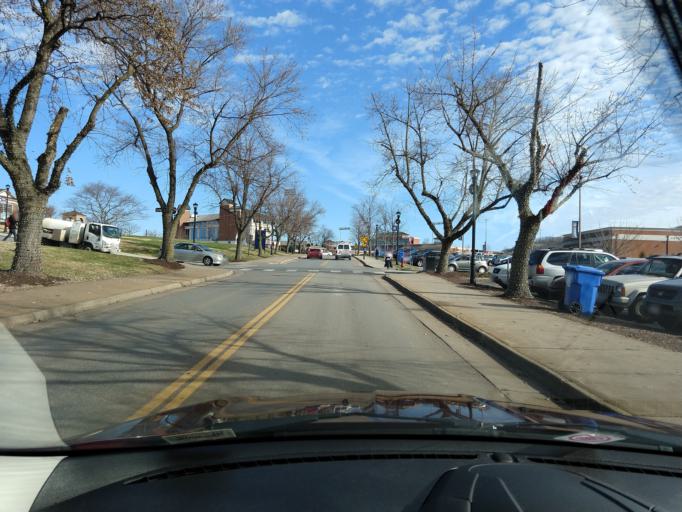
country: US
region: Virginia
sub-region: City of Lynchburg
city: West Lynchburg
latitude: 37.3521
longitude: -79.1773
